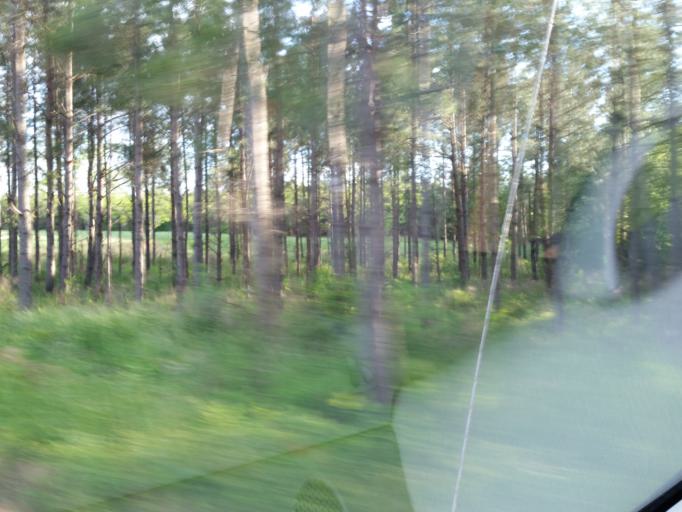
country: US
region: Georgia
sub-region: Turner County
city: Ashburn
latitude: 31.6581
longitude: -83.6311
